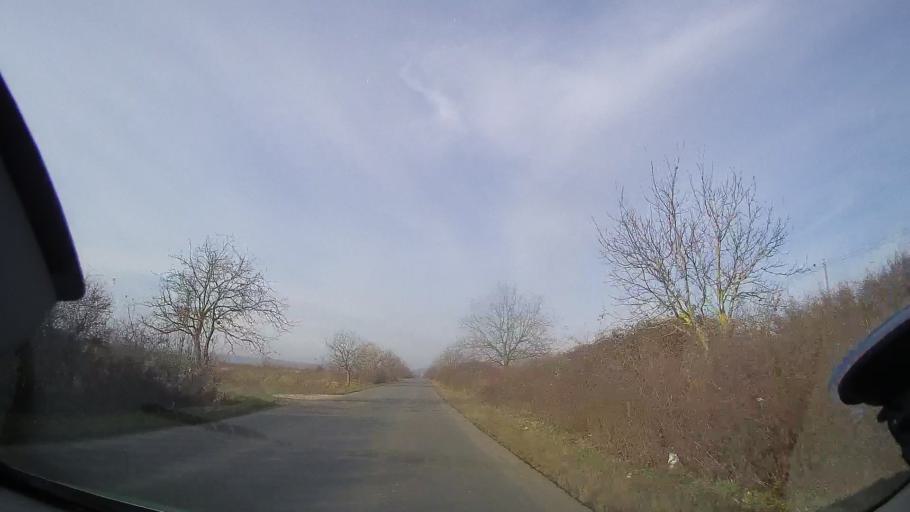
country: RO
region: Bihor
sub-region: Comuna Spinus
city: Spinus
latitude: 47.2217
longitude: 22.1710
